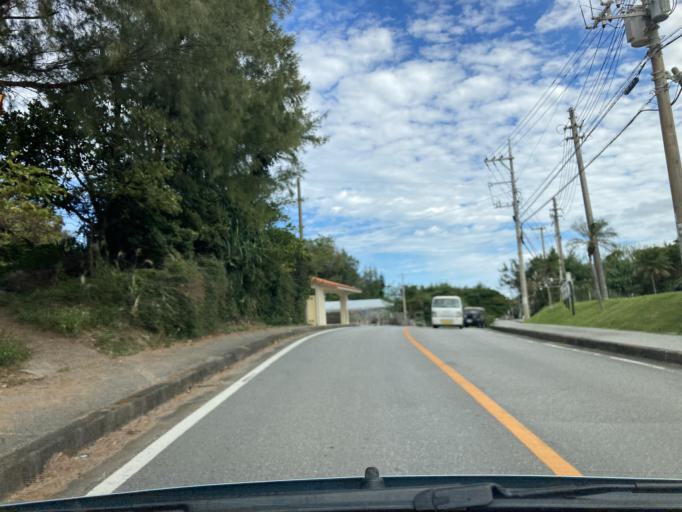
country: JP
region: Okinawa
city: Ishikawa
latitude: 26.4240
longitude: 127.7457
